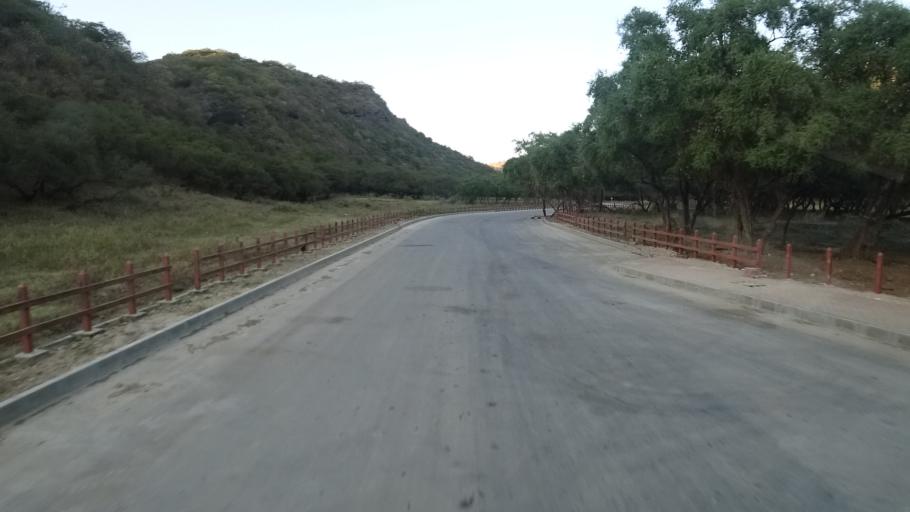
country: OM
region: Zufar
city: Salalah
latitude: 17.0981
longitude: 54.4500
